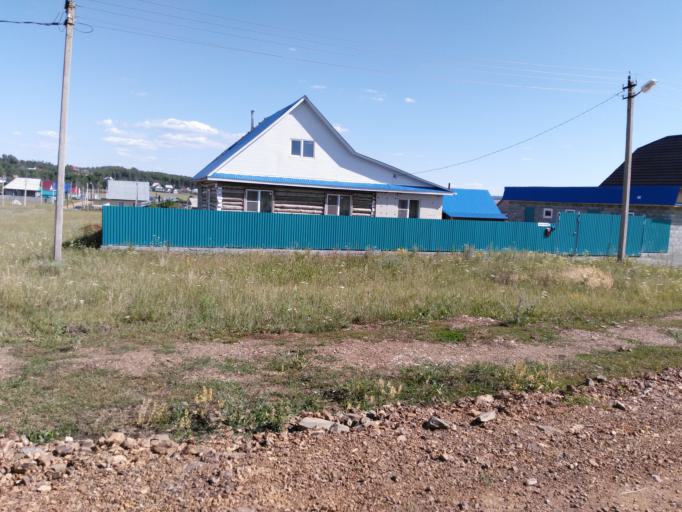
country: RU
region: Bashkortostan
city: Uchaly
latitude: 54.2917
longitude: 59.3593
